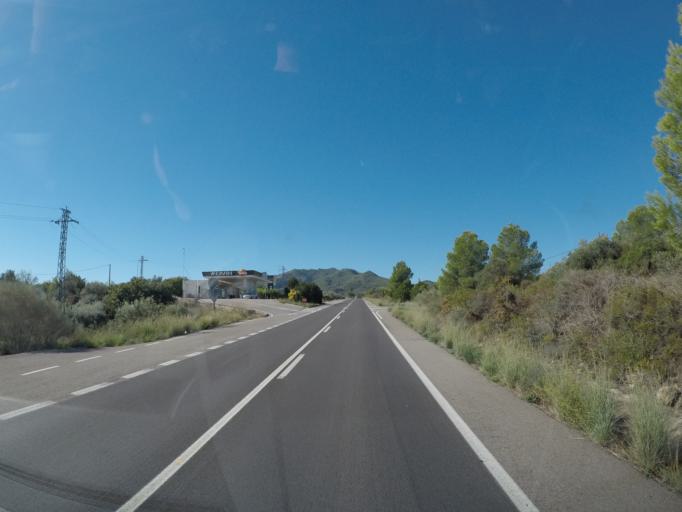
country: ES
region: Catalonia
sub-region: Provincia de Tarragona
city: Rasquera
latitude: 41.0137
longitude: 0.6107
